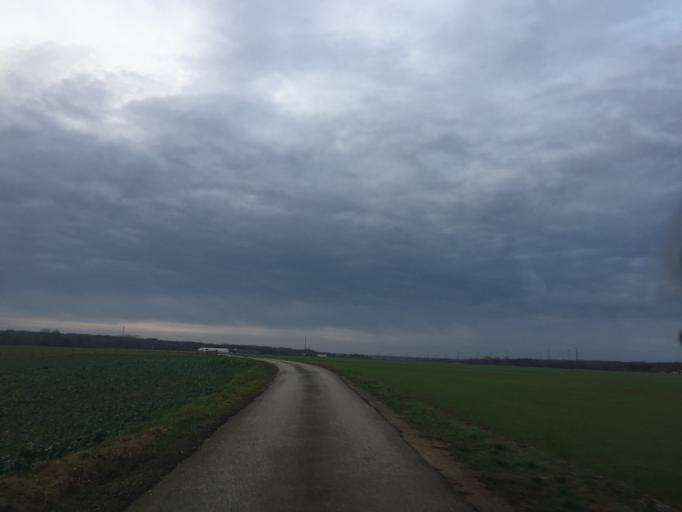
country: FR
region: Franche-Comte
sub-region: Departement du Jura
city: Mont-sous-Vaudrey
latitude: 46.9443
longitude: 5.6671
